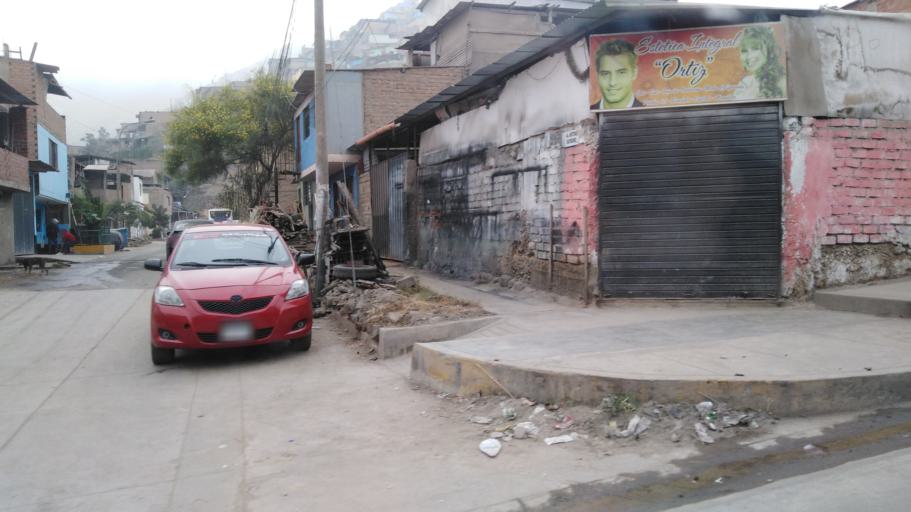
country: PE
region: Lima
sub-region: Lima
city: La Molina
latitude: -12.1434
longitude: -76.9389
